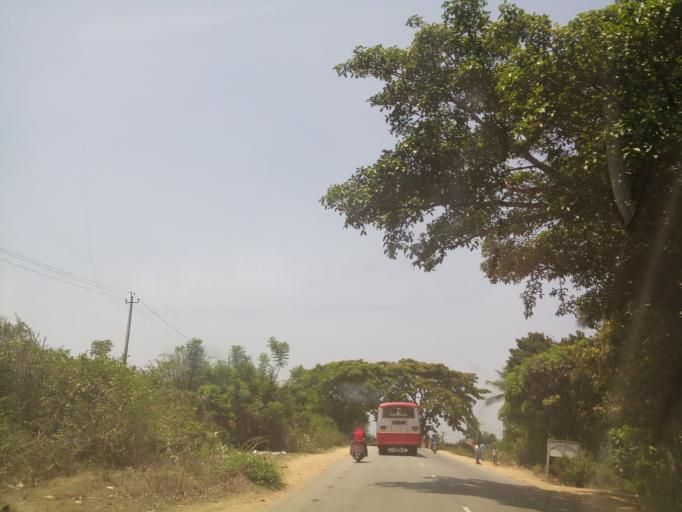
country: IN
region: Karnataka
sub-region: Hassan
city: Alur
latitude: 12.9447
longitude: 75.8947
